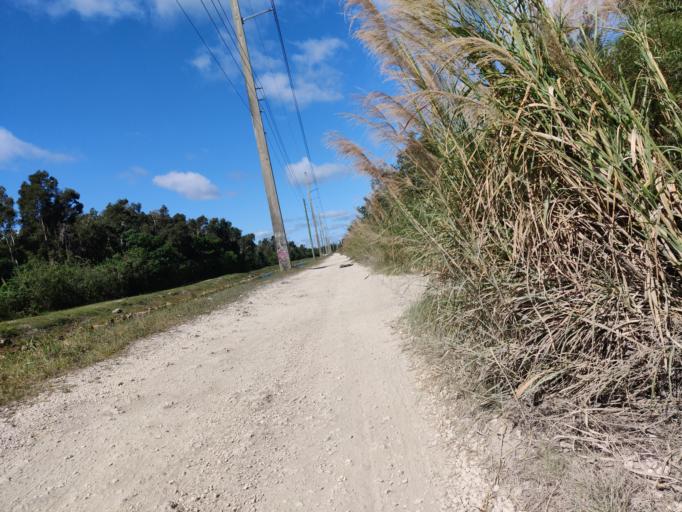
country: US
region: Florida
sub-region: Miami-Dade County
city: Kendall West
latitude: 25.7272
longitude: -80.4731
